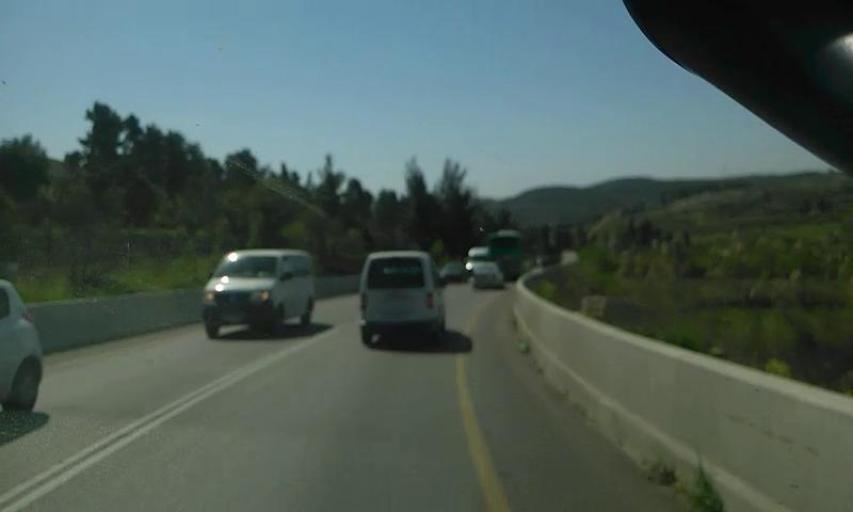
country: PS
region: West Bank
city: Shuyukh al `Arrub
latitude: 31.6369
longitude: 35.1327
